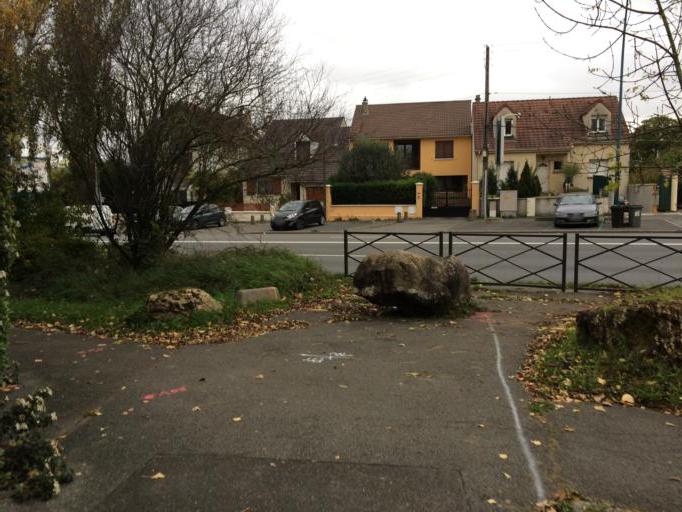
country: FR
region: Ile-de-France
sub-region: Departement des Hauts-de-Seine
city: Antony
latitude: 48.7340
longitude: 2.3008
